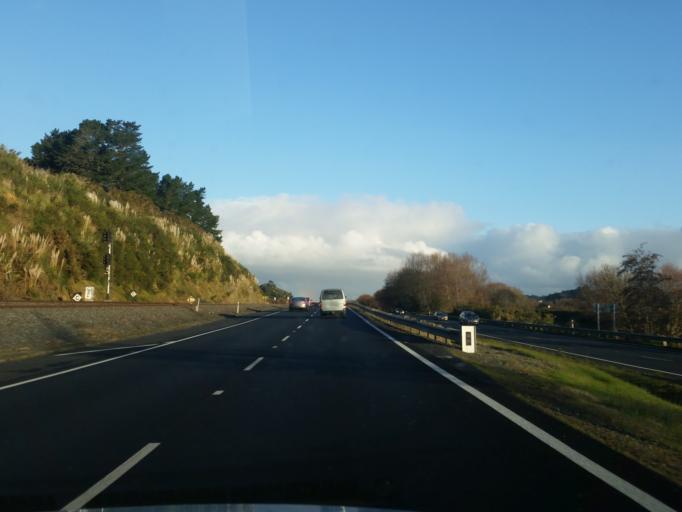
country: NZ
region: Auckland
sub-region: Auckland
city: Pukekohe East
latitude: -37.2677
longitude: 175.0453
